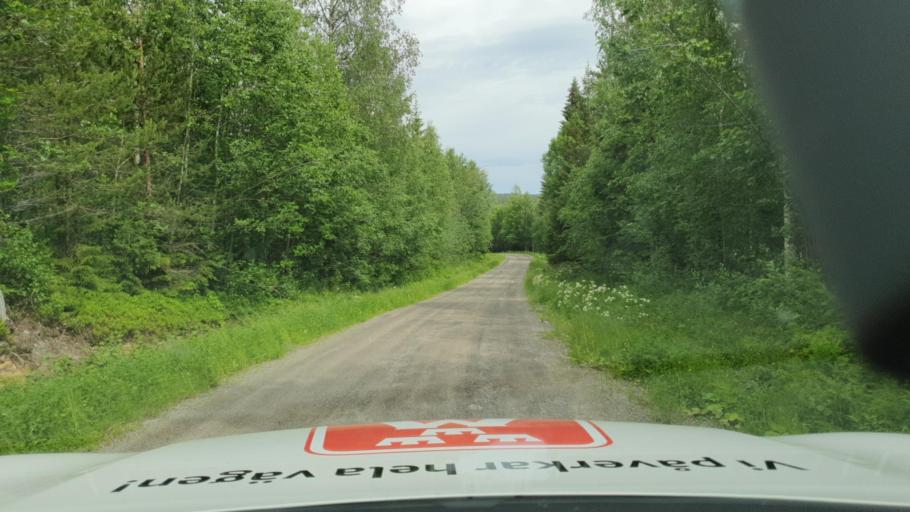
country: SE
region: Vaesterbotten
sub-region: Robertsfors Kommun
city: Robertsfors
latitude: 64.2665
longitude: 20.6897
